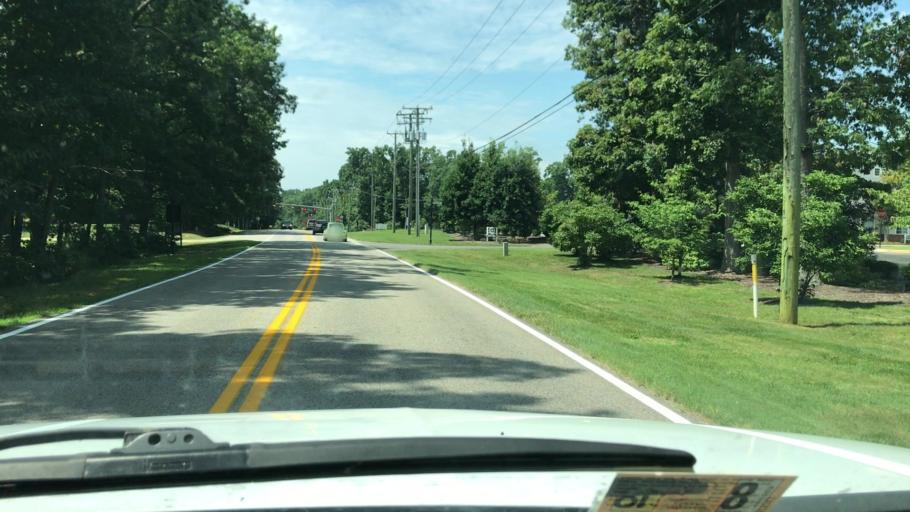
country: US
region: Virginia
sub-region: Chesterfield County
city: Brandermill
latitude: 37.5248
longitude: -77.6632
